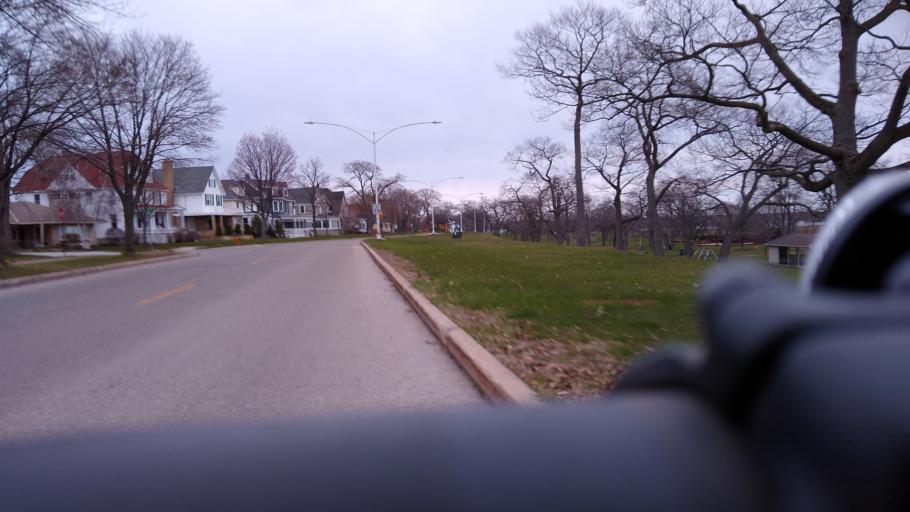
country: US
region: Michigan
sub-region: Delta County
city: Escanaba
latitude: 45.7392
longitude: -87.0561
